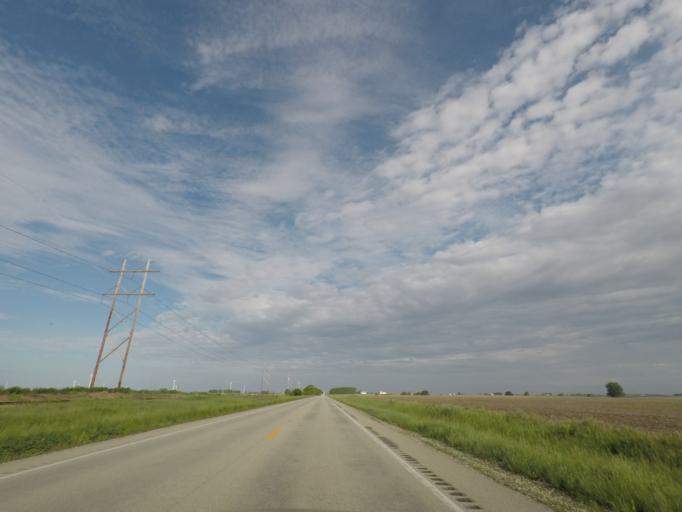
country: US
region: Illinois
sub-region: Logan County
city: Mount Pulaski
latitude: 39.9765
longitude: -89.1959
